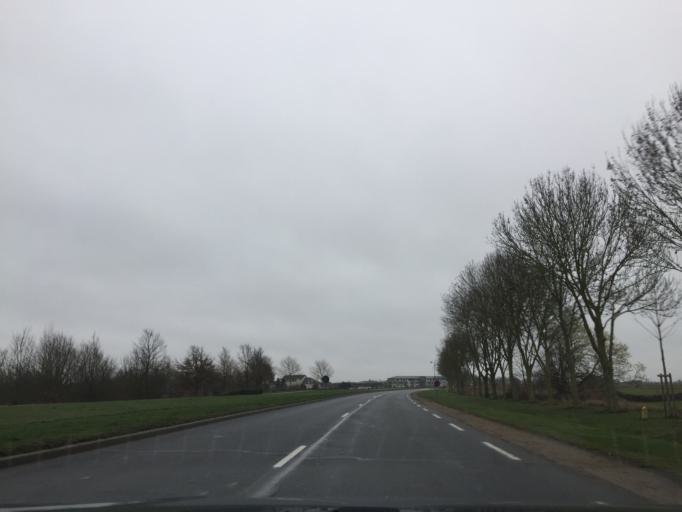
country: FR
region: Ile-de-France
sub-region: Departement de Seine-et-Marne
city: Magny-le-Hongre
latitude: 48.8717
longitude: 2.8052
